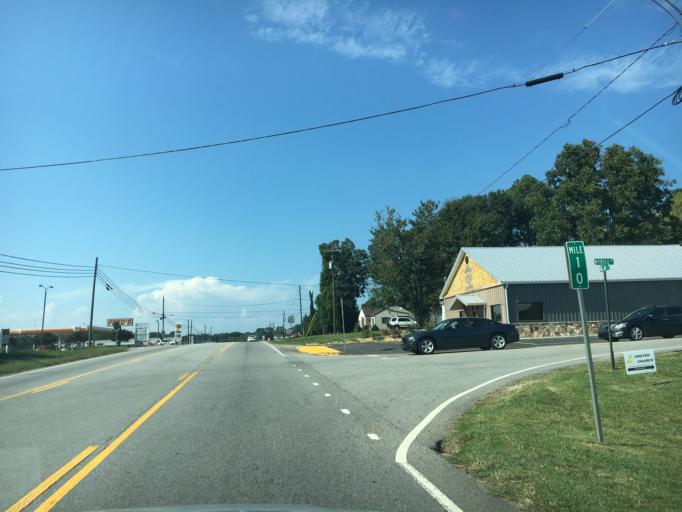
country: US
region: Georgia
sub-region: Franklin County
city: Lavonia
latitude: 34.4216
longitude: -83.1024
